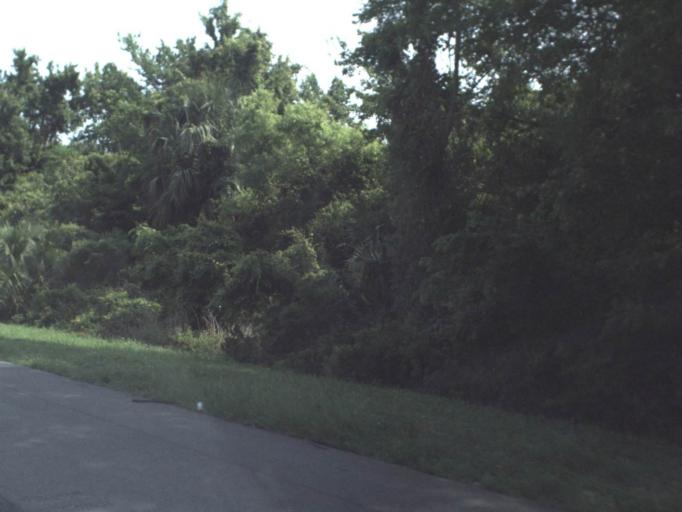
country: US
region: Florida
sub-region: Nassau County
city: Yulee
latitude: 30.5613
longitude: -81.6421
